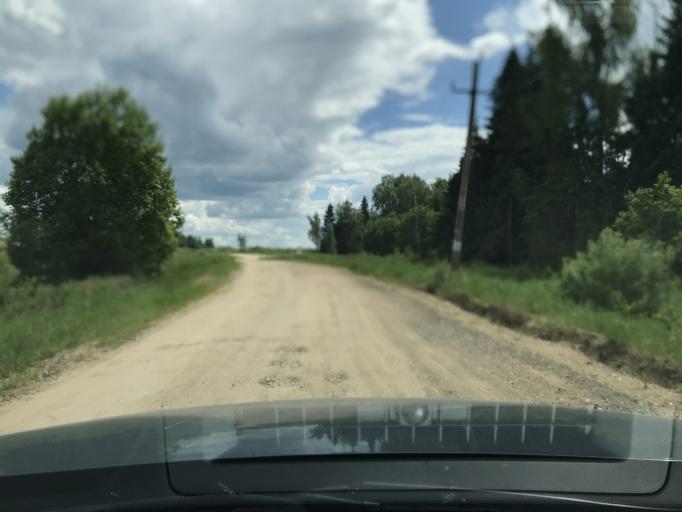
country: RU
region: Moskovskaya
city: Vereya
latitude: 55.3188
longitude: 36.3223
